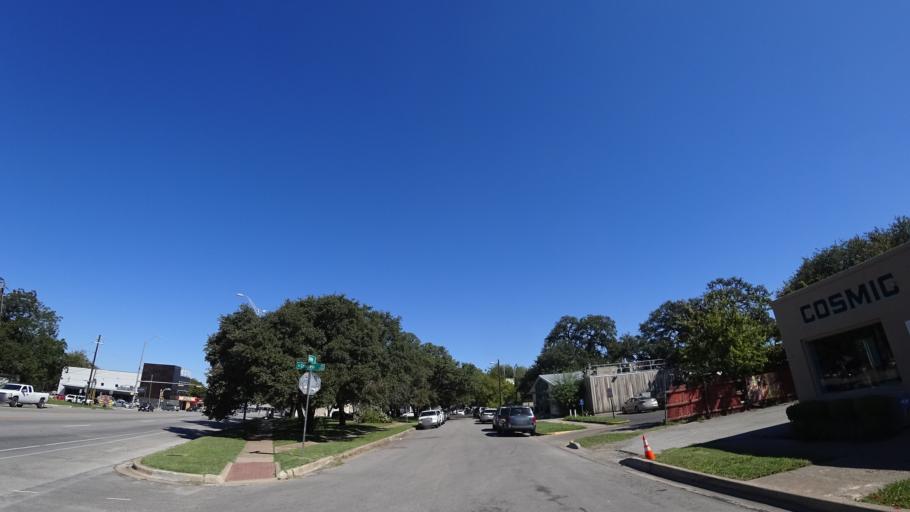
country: US
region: Texas
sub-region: Travis County
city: Austin
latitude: 30.2410
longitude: -97.7525
